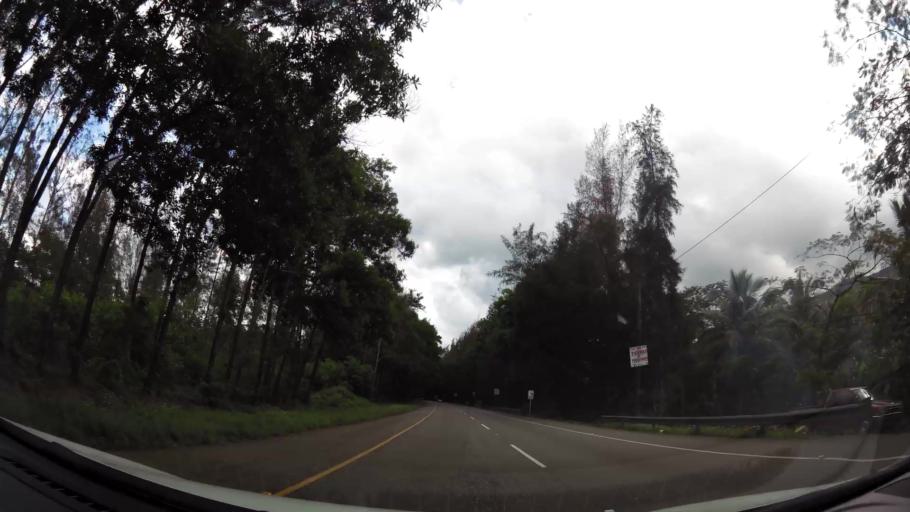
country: DO
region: La Vega
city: Rincon
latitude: 19.1260
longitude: -70.4539
